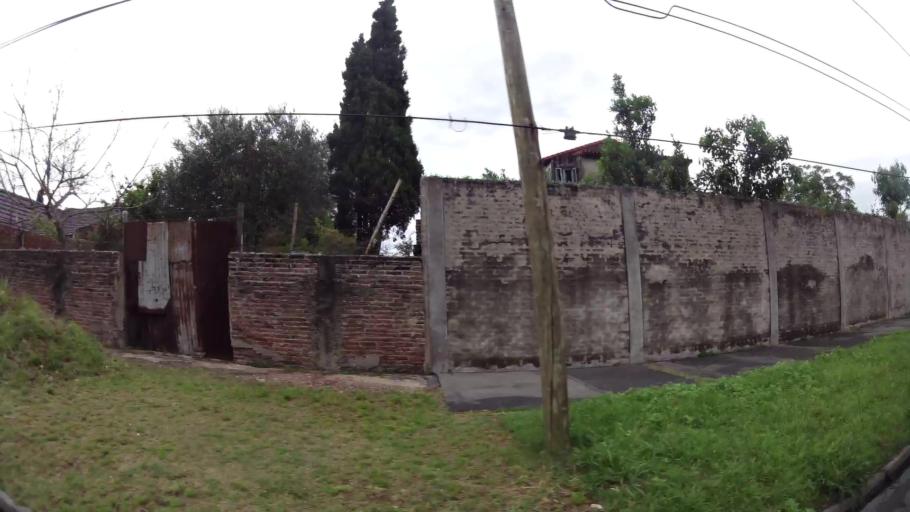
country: AR
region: Buenos Aires
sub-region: Partido de Lanus
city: Lanus
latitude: -34.7241
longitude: -58.3800
